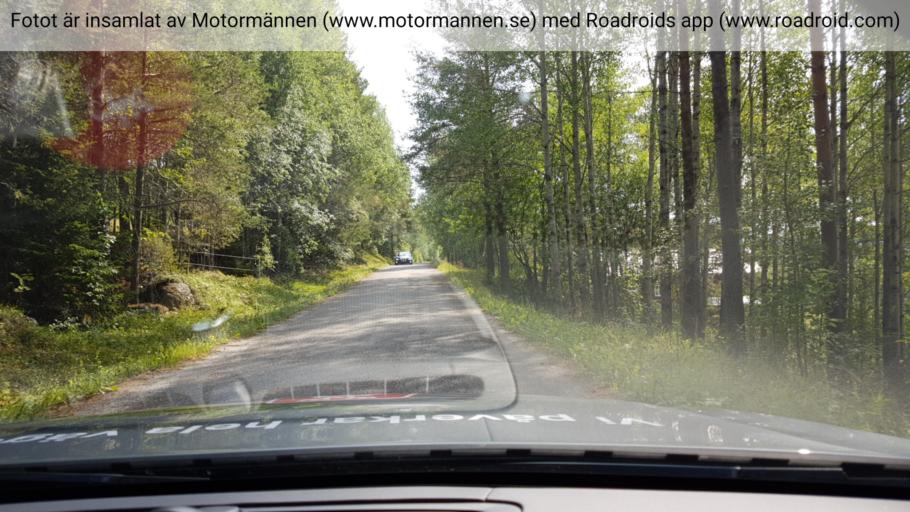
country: SE
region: Jaemtland
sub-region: OEstersunds Kommun
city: Brunflo
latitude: 63.0117
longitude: 15.1019
